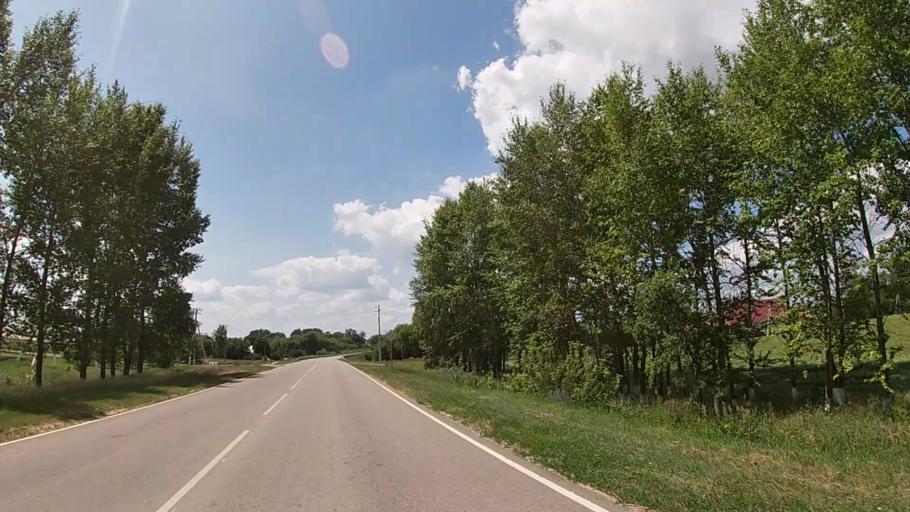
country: RU
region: Belgorod
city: Grayvoron
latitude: 50.4371
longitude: 35.6059
